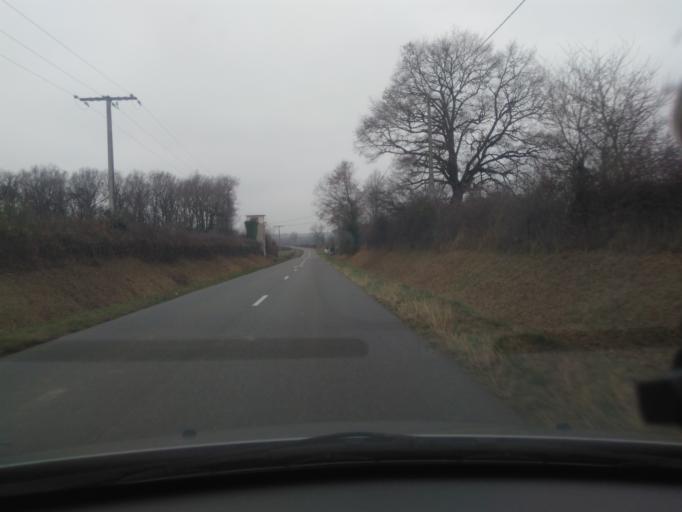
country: FR
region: Centre
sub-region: Departement du Cher
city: Le Chatelet
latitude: 46.6423
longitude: 2.3183
